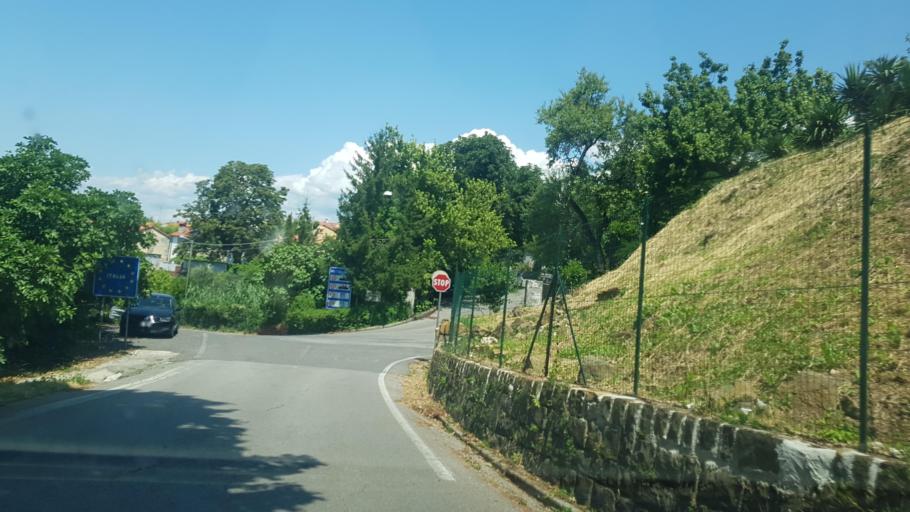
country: SI
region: Koper-Capodistria
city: Hrvatini
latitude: 45.5856
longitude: 13.7769
